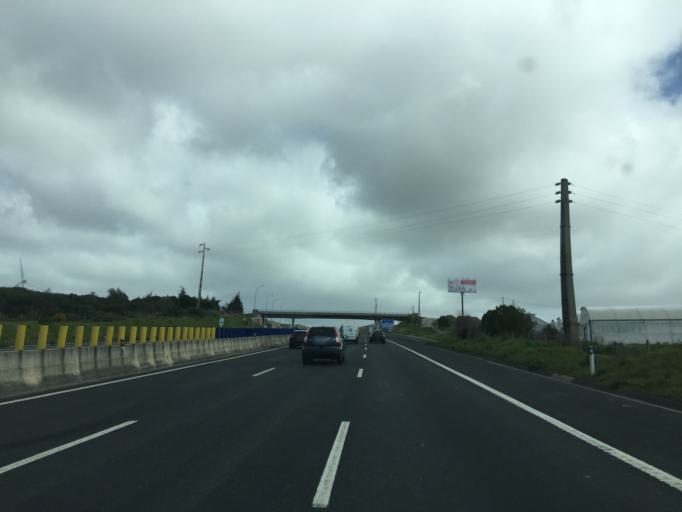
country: PT
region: Lisbon
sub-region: Loures
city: Loures
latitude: 38.8782
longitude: -9.1987
